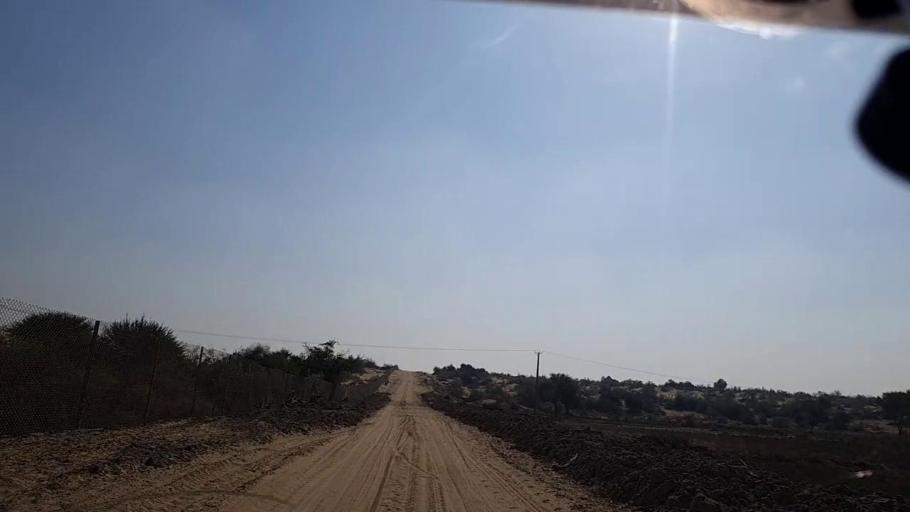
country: PK
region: Sindh
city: Khanpur
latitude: 27.5652
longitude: 69.3888
